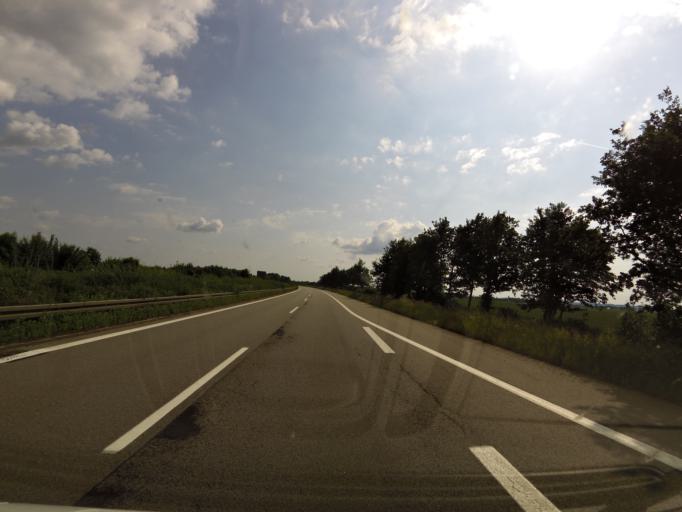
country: DE
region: Bavaria
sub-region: Lower Bavaria
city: Wallersdorf
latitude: 48.7433
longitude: 12.7385
